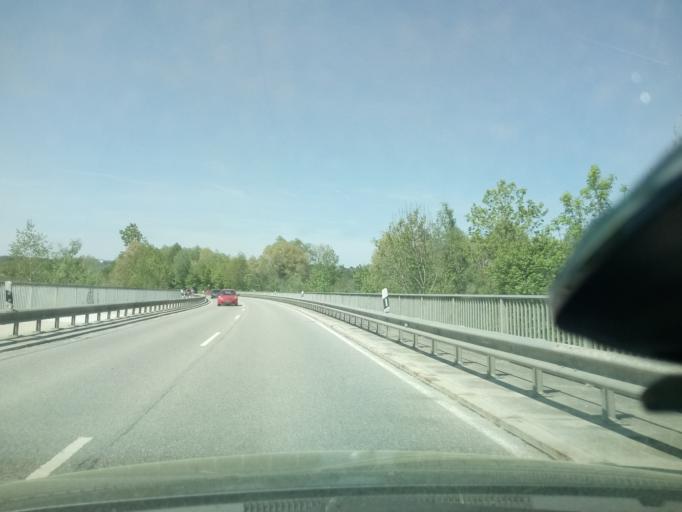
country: DE
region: Bavaria
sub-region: Upper Bavaria
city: Kraiburg am Inn
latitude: 48.1934
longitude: 12.4307
